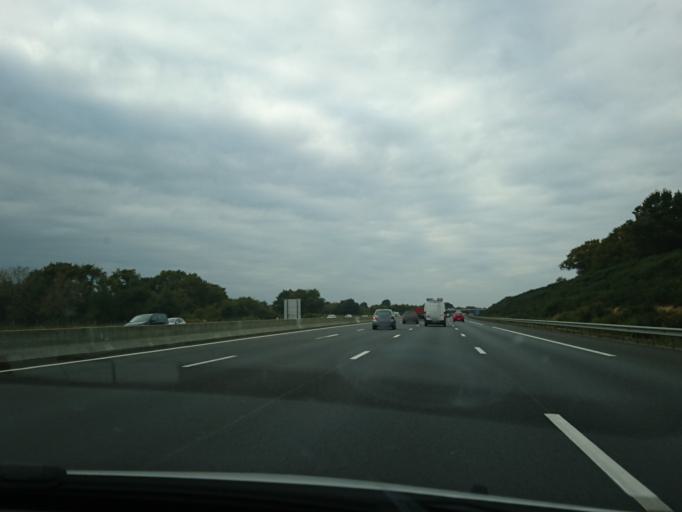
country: FR
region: Pays de la Loire
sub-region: Departement de la Loire-Atlantique
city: Sautron
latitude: 47.2592
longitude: -1.6956
